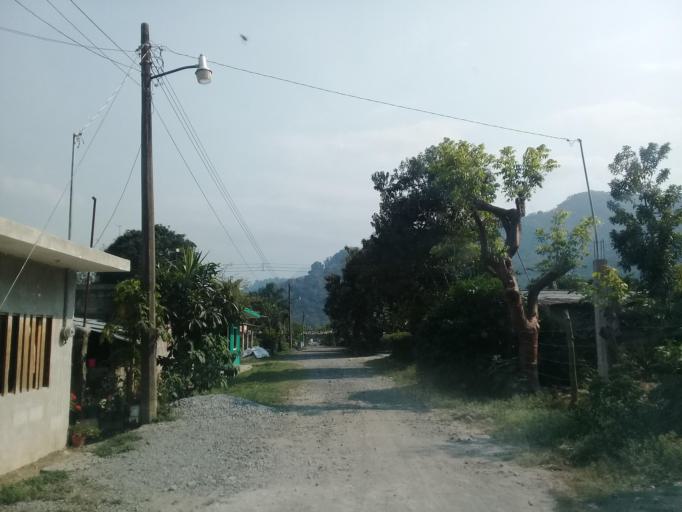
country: MX
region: Veracruz
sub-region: Ixtaczoquitlan
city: Campo Chico
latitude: 18.8380
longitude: -97.0272
